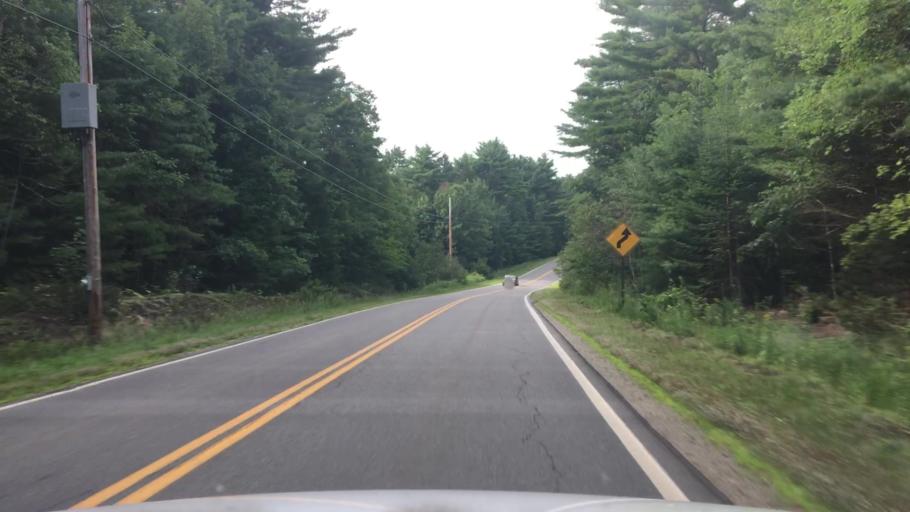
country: US
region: Maine
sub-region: Lincoln County
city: Jefferson
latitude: 44.2007
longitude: -69.3816
